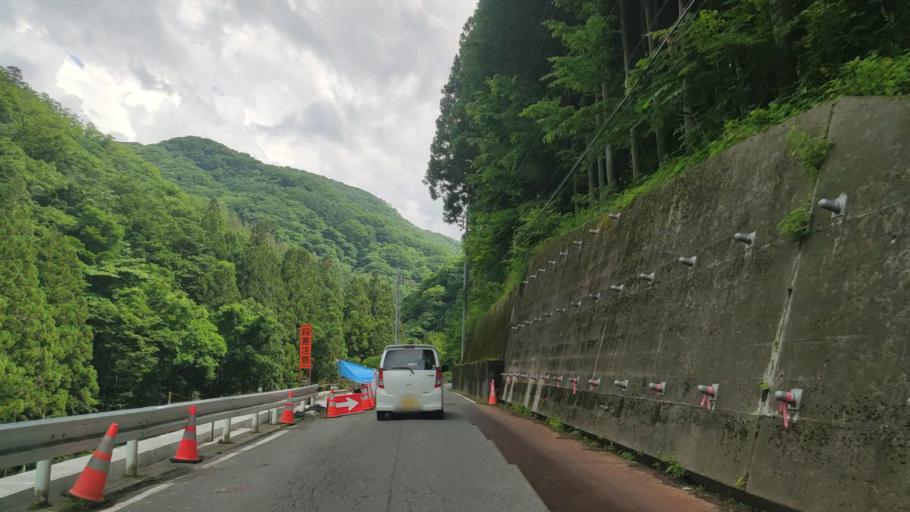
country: JP
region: Gunma
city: Tomioka
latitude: 36.1025
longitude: 138.7172
